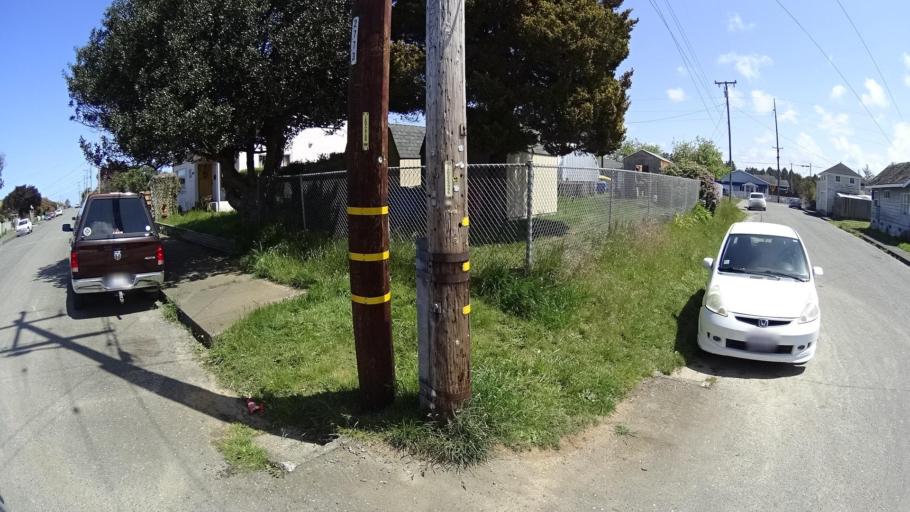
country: US
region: California
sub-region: Humboldt County
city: Bayview
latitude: 40.7750
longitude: -124.1726
